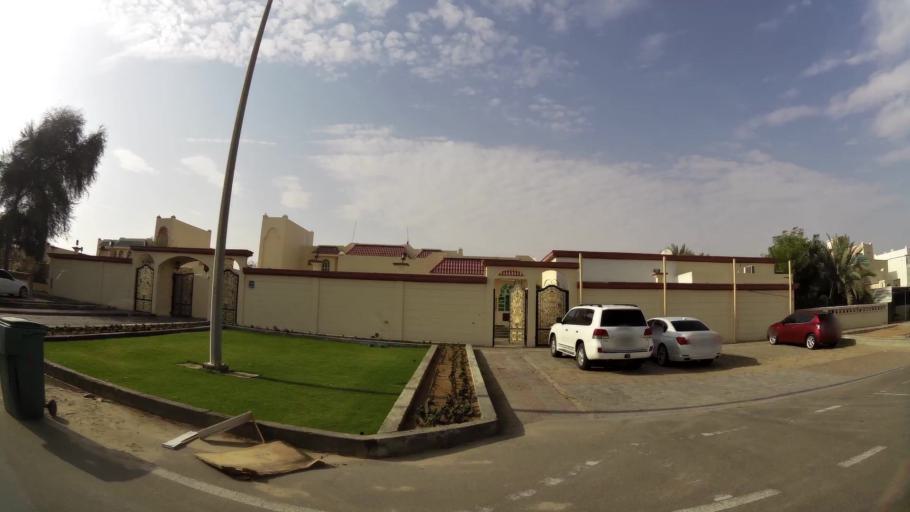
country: AE
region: Abu Dhabi
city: Abu Dhabi
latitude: 24.2612
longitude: 54.6722
